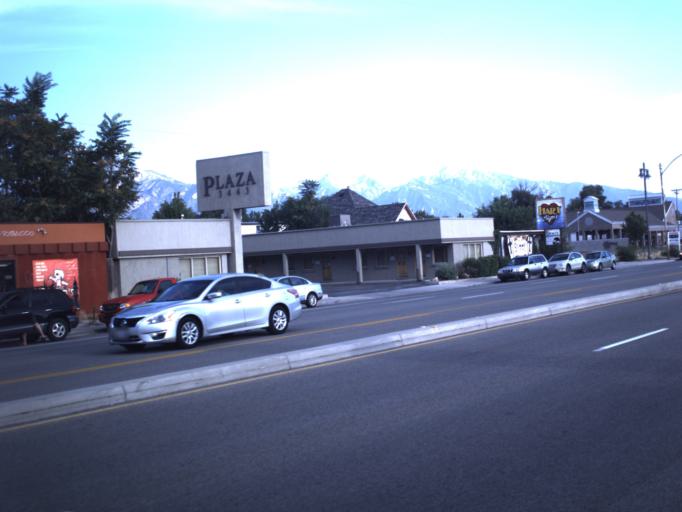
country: US
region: Utah
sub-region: Salt Lake County
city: Centerfield
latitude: 40.6968
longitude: -111.8884
